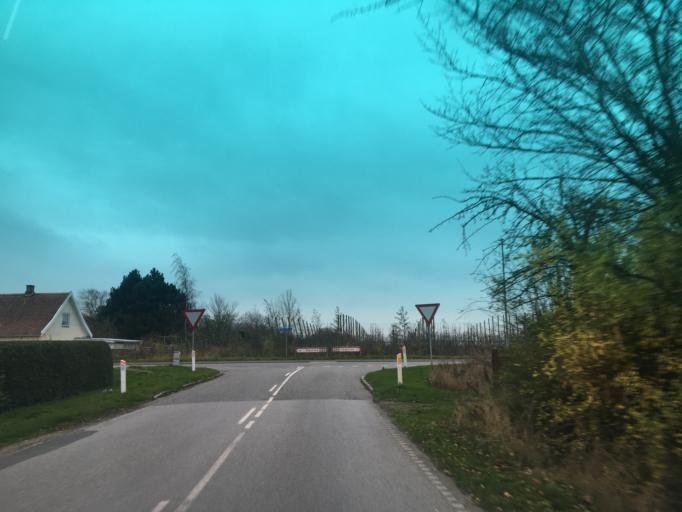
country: DK
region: Zealand
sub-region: Slagelse Kommune
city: Skaelskor
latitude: 55.2394
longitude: 11.4240
